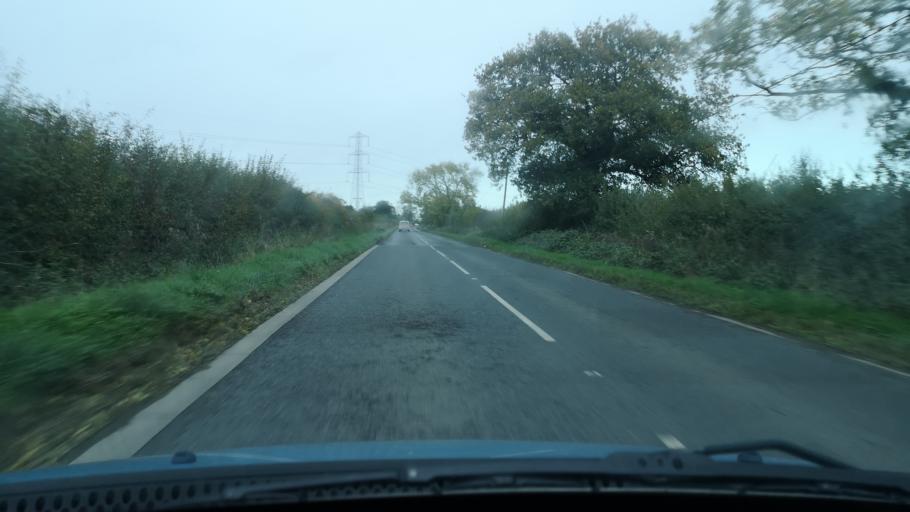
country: GB
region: England
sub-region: Doncaster
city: Moss
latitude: 53.6193
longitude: -1.0788
